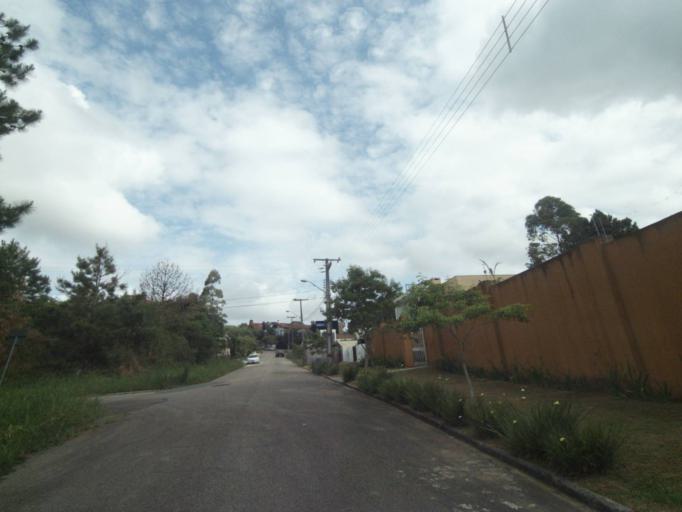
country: BR
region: Parana
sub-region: Curitiba
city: Curitiba
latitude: -25.3801
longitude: -49.2883
